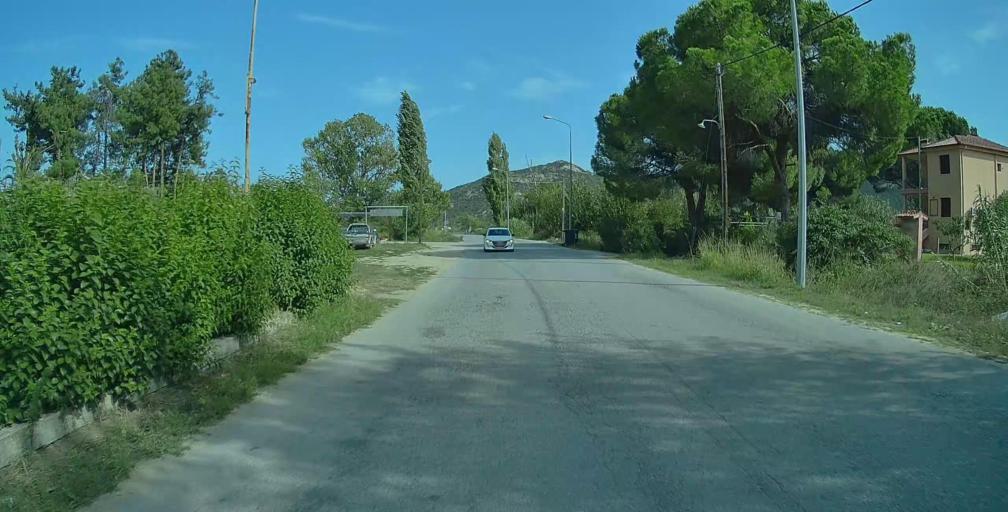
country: GR
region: Central Macedonia
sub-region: Nomos Chalkidikis
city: Sykia
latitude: 40.0340
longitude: 23.9619
